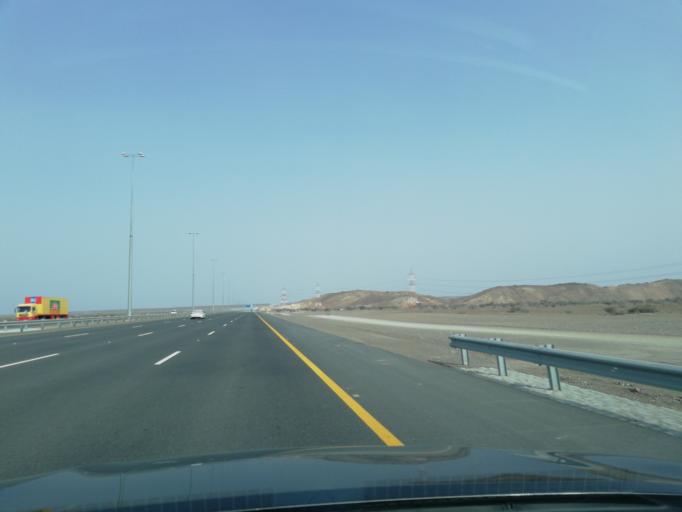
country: OM
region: Al Batinah
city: Al Sohar
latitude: 24.3028
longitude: 56.6000
